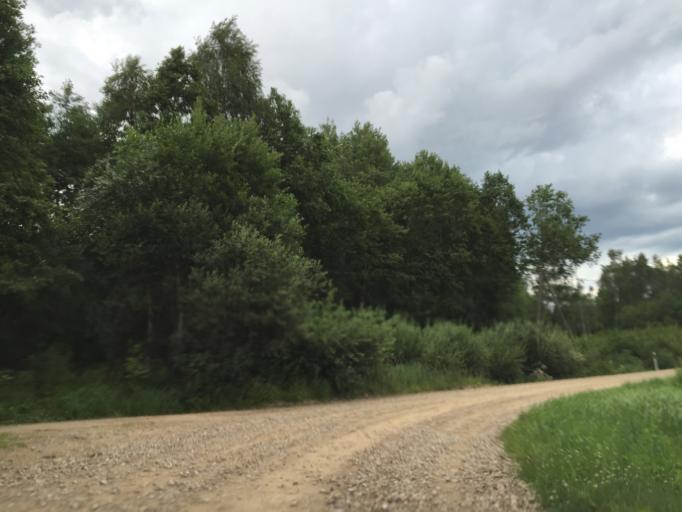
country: LV
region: Malpils
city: Malpils
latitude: 56.9127
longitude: 24.9855
